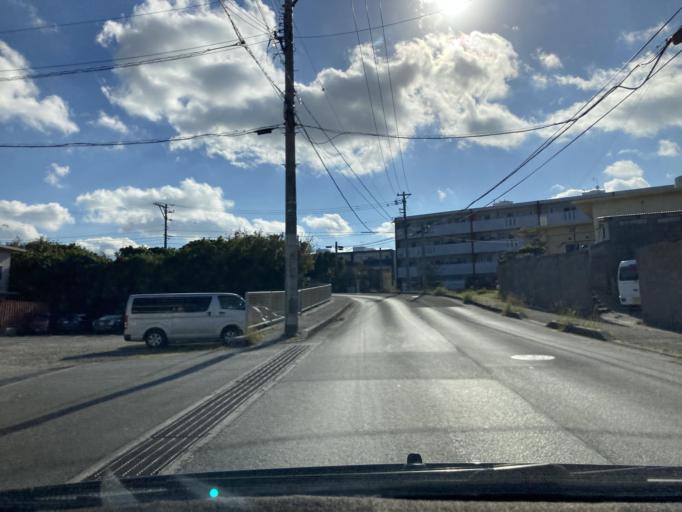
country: JP
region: Okinawa
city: Katsuren-haebaru
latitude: 26.3123
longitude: 127.9103
